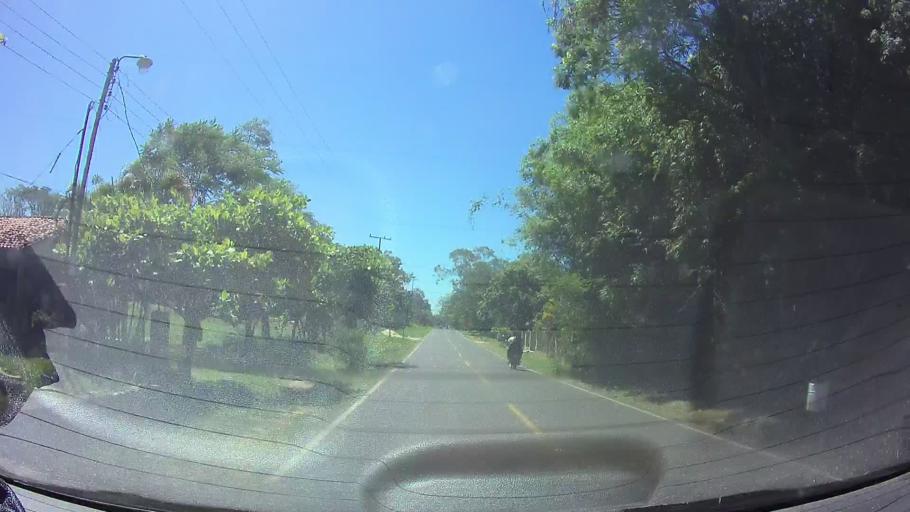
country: PY
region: Central
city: Aregua
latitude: -25.2740
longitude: -57.4084
